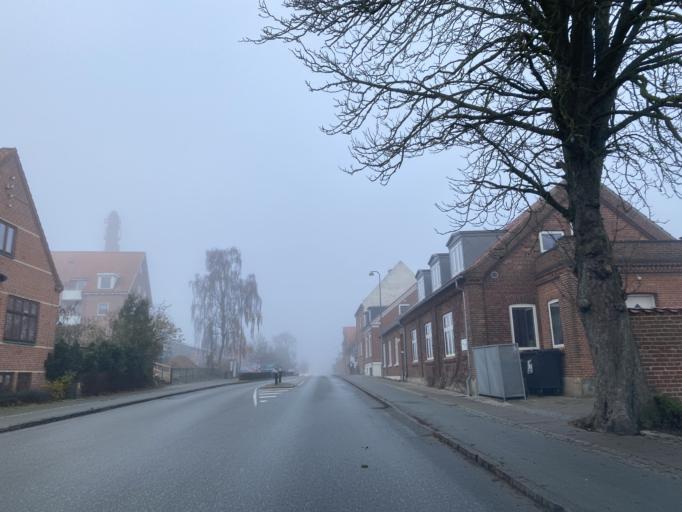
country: DK
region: Central Jutland
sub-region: Skanderborg Kommune
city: Skanderborg
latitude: 56.0358
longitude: 9.9283
